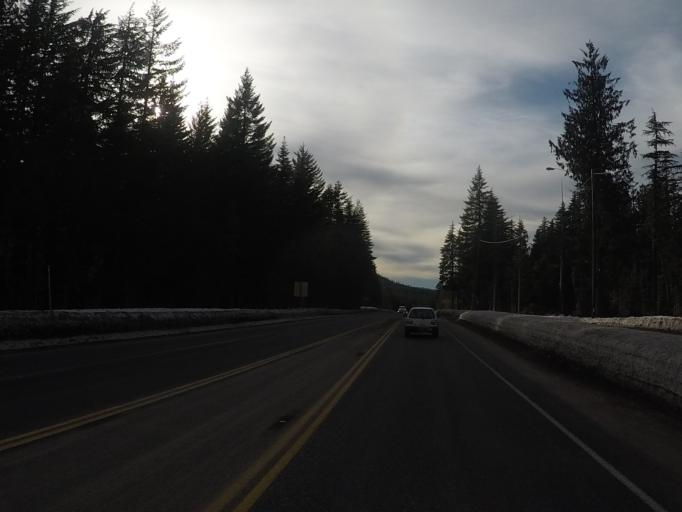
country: US
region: Oregon
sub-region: Clackamas County
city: Mount Hood Village
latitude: 45.3029
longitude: -121.7722
